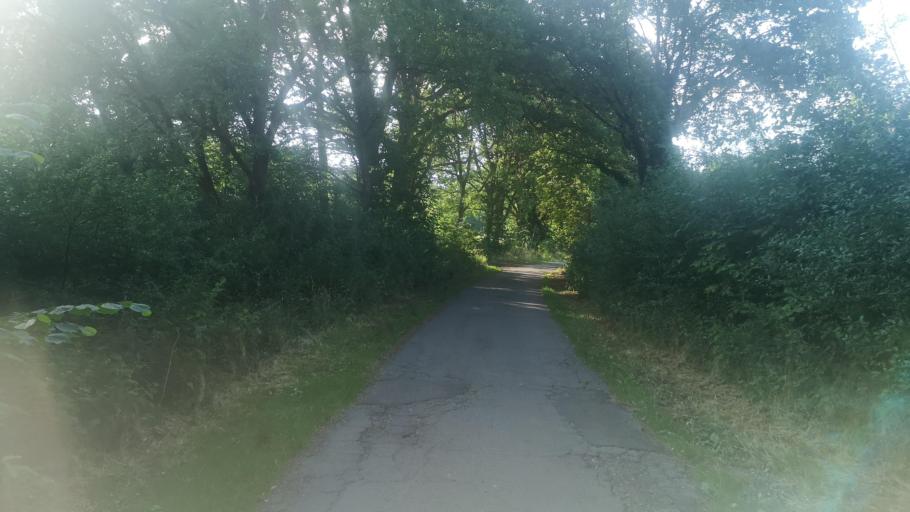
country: DE
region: Lower Saxony
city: Dahlenburg
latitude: 53.2065
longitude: 10.7157
